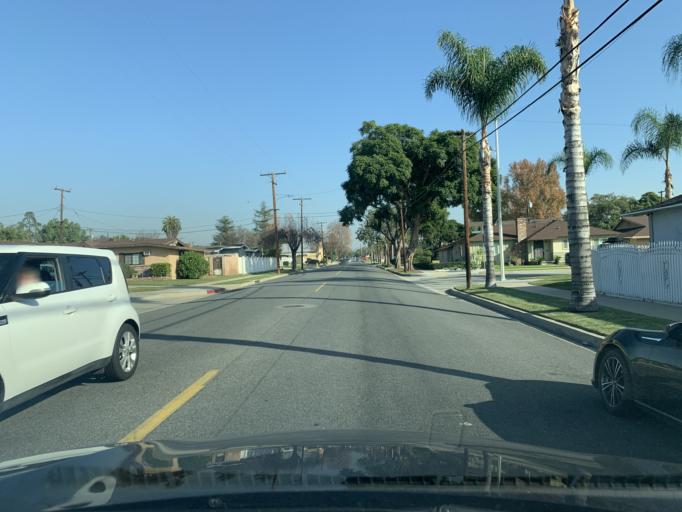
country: US
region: California
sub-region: Los Angeles County
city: Covina
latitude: 34.0826
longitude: -117.8965
